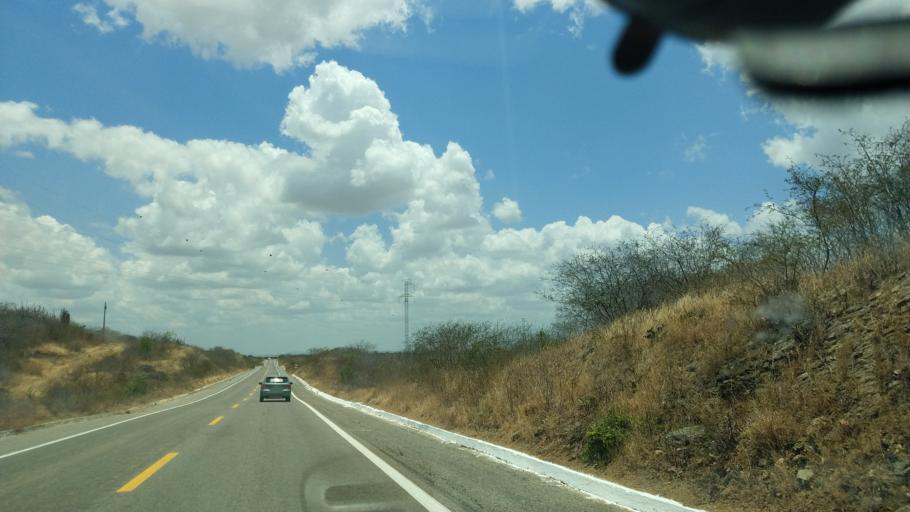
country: BR
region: Rio Grande do Norte
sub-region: Cerro Cora
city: Cerro Cora
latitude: -6.1931
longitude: -36.2601
